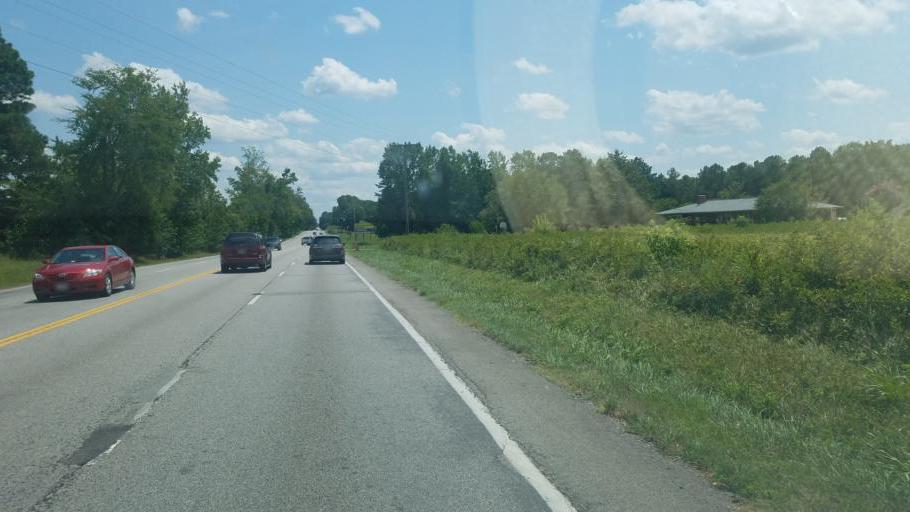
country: US
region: Virginia
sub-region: Prince George County
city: Prince George
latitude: 37.1397
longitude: -77.2503
